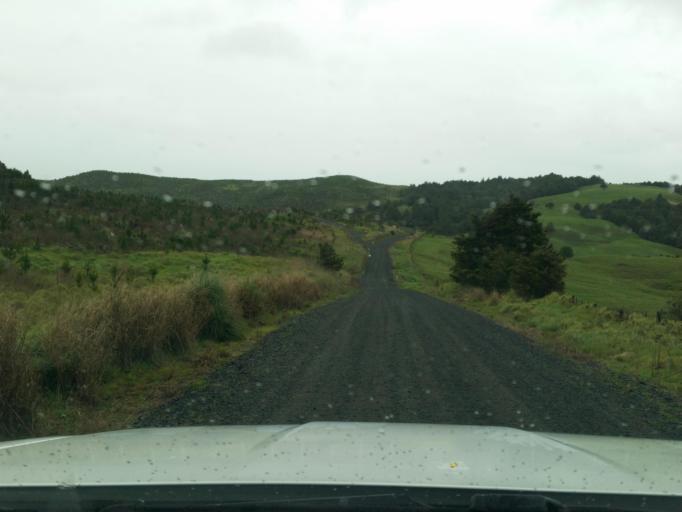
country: NZ
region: Northland
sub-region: Kaipara District
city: Dargaville
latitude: -35.8554
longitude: 173.8786
